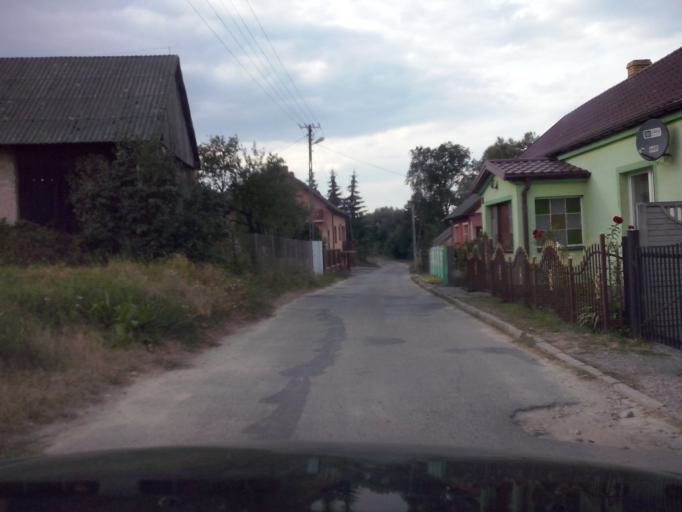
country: PL
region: Swietokrzyskie
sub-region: Powiat kielecki
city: Rakow
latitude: 50.6716
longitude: 21.0406
